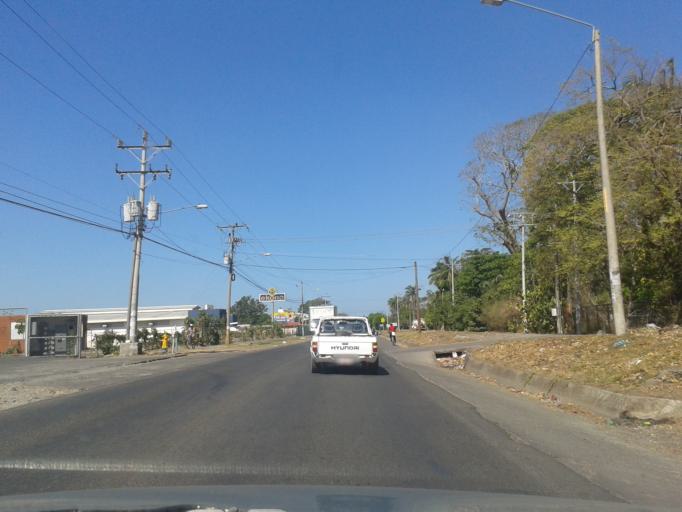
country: CR
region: Puntarenas
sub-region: Canton Central de Puntarenas
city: Chacarita
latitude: 9.9779
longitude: -84.7280
